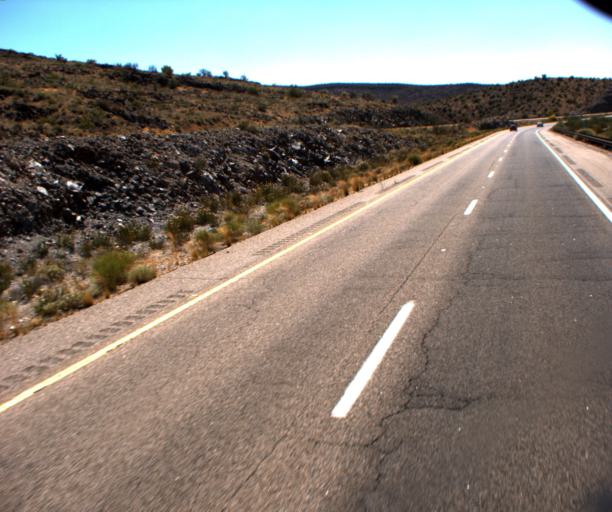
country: US
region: Arizona
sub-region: Yavapai County
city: Bagdad
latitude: 34.5712
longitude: -113.4791
